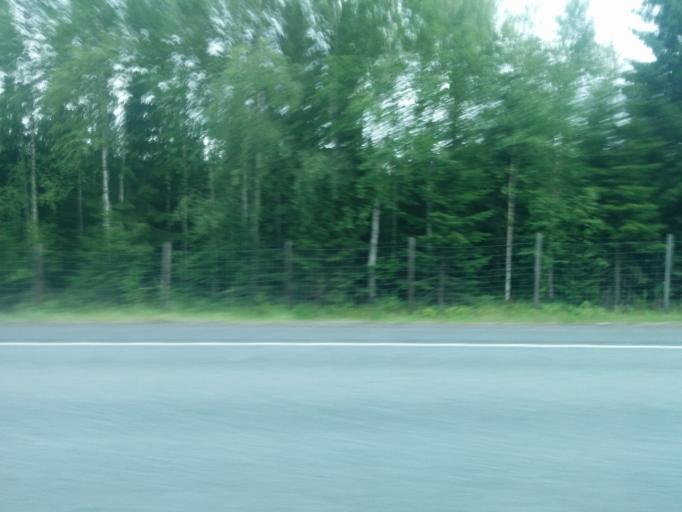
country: FI
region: Pirkanmaa
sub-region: Tampere
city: Orivesi
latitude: 61.6628
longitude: 24.2640
